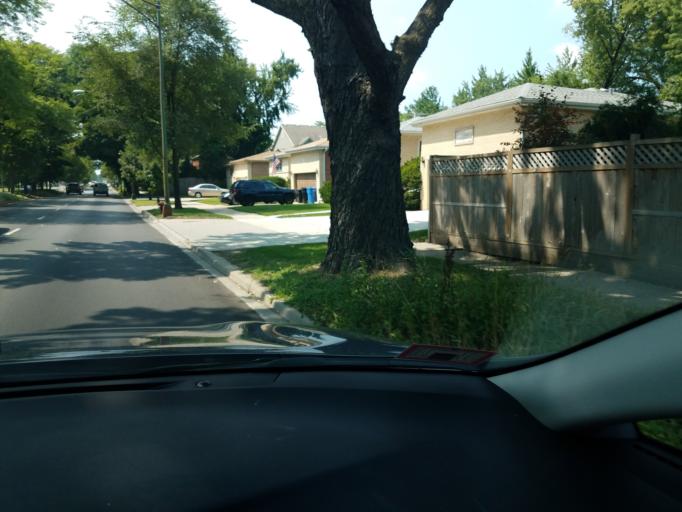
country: US
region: Illinois
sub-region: Cook County
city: Lincolnwood
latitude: 41.9900
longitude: -87.7432
